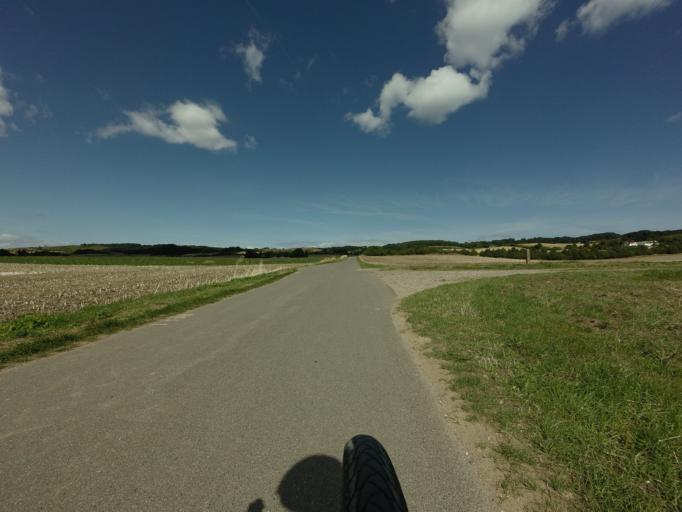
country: DK
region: Zealand
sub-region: Vordingborg Kommune
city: Stege
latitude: 54.9494
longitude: 12.5324
